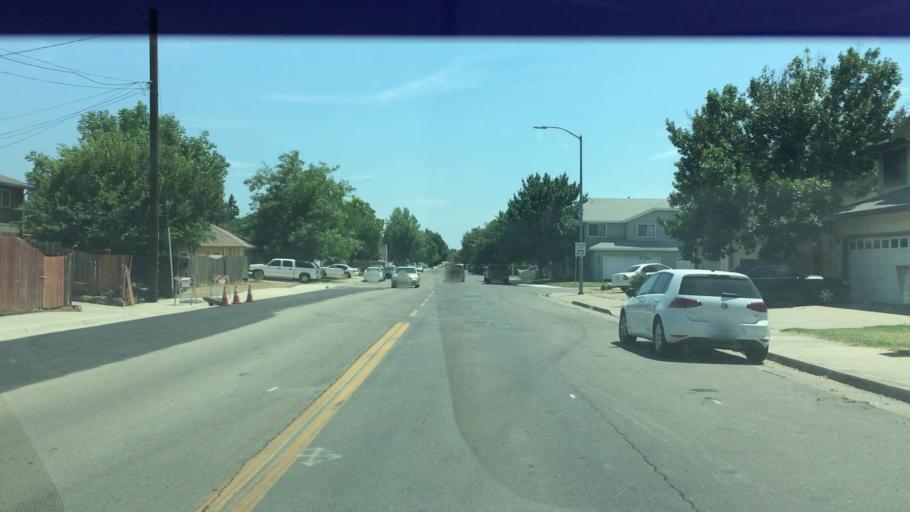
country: US
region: California
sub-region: Sacramento County
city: Galt
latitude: 38.2471
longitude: -121.3094
